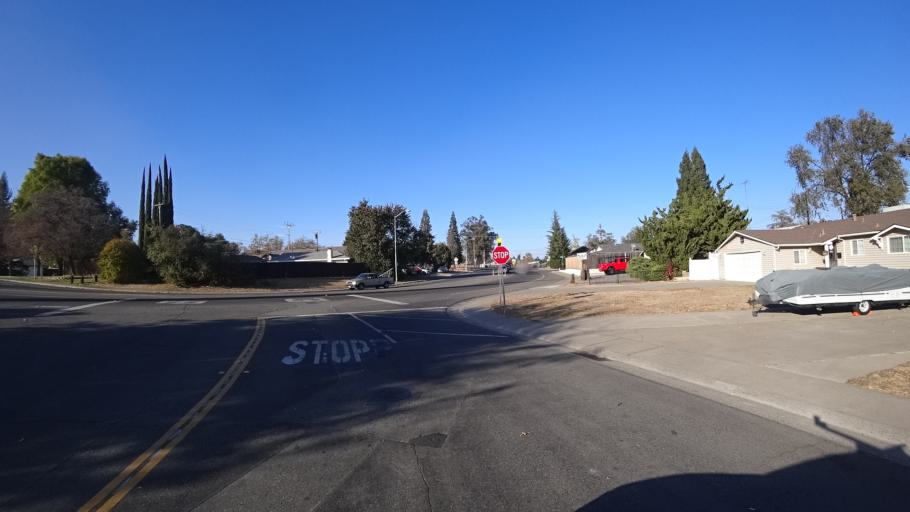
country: US
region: California
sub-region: Sacramento County
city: Antelope
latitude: 38.7060
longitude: -121.3058
